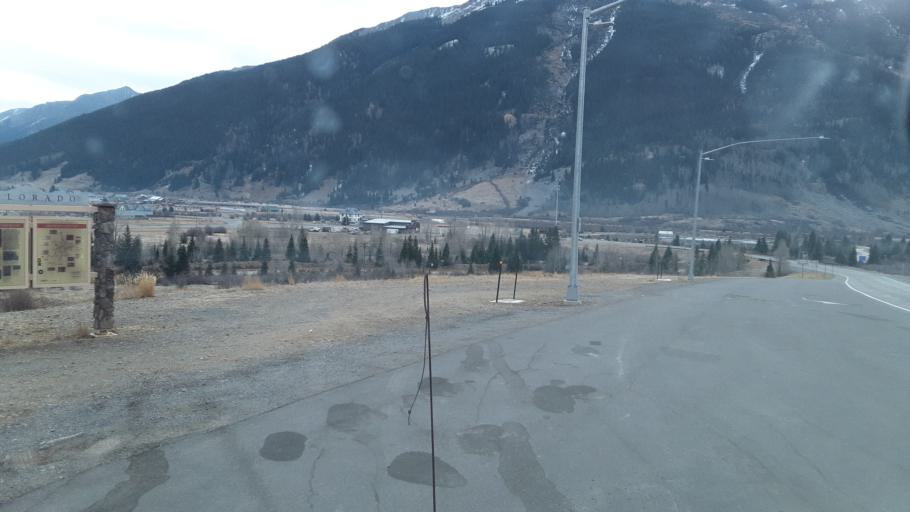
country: US
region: Colorado
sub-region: San Juan County
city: Silverton
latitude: 37.8049
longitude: -107.6763
